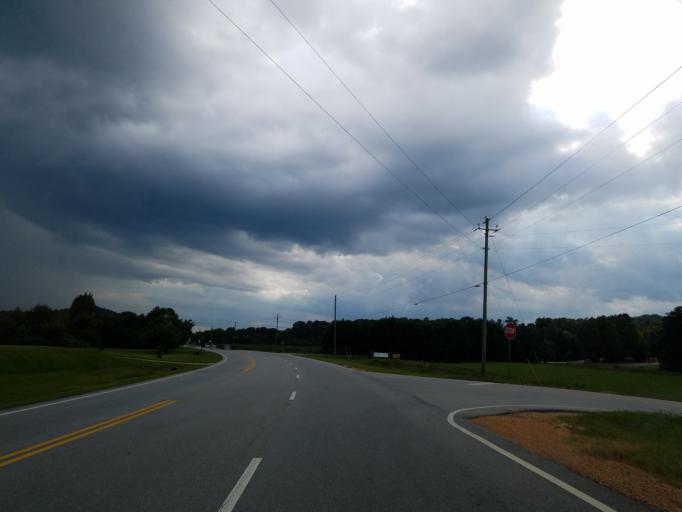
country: US
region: Georgia
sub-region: Floyd County
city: Shannon
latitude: 34.3701
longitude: -85.0700
